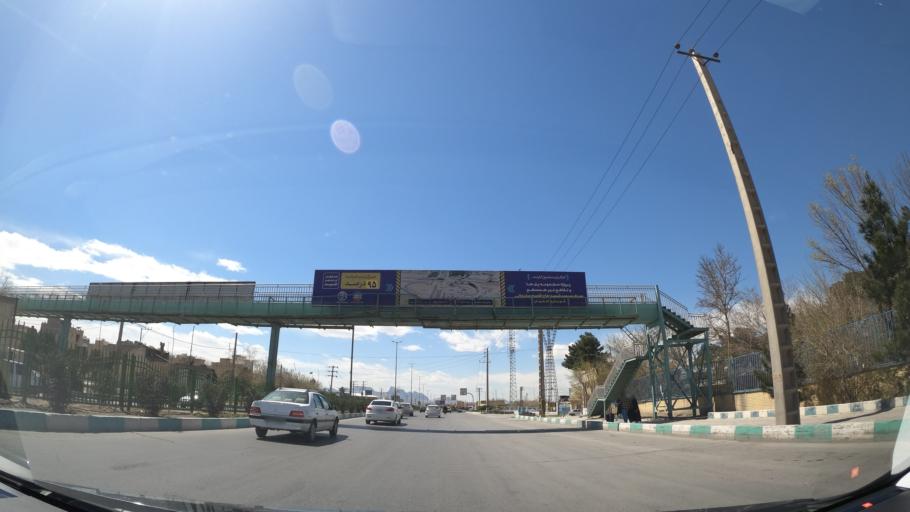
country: IR
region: Isfahan
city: Isfahan
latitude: 32.6479
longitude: 51.7858
